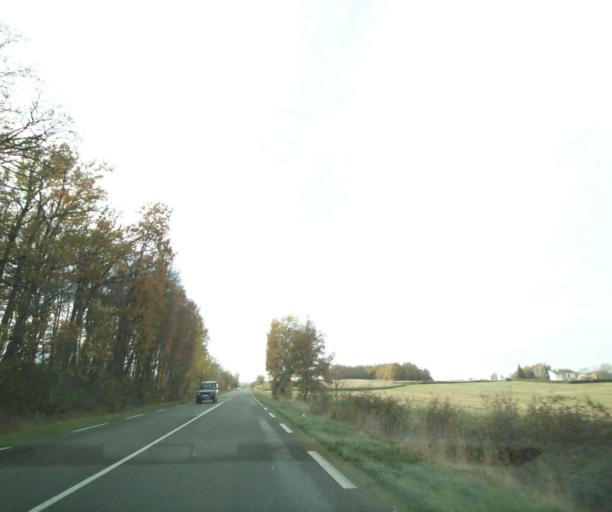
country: FR
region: Midi-Pyrenees
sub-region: Departement du Gers
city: Vic-Fezensac
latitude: 43.7545
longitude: 0.2506
